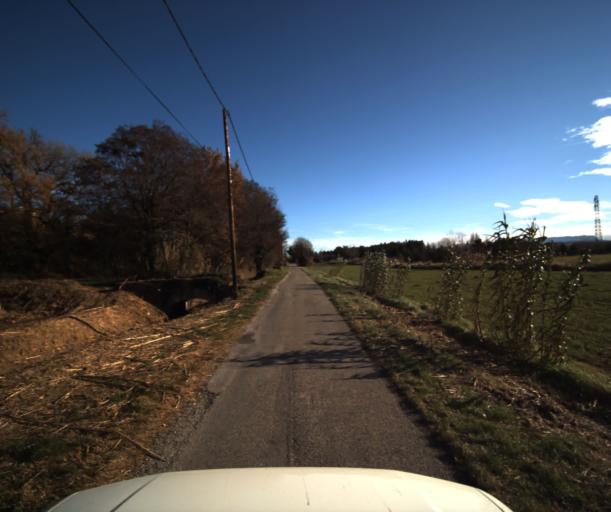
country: FR
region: Provence-Alpes-Cote d'Azur
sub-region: Departement du Vaucluse
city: Pertuis
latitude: 43.6936
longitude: 5.4828
